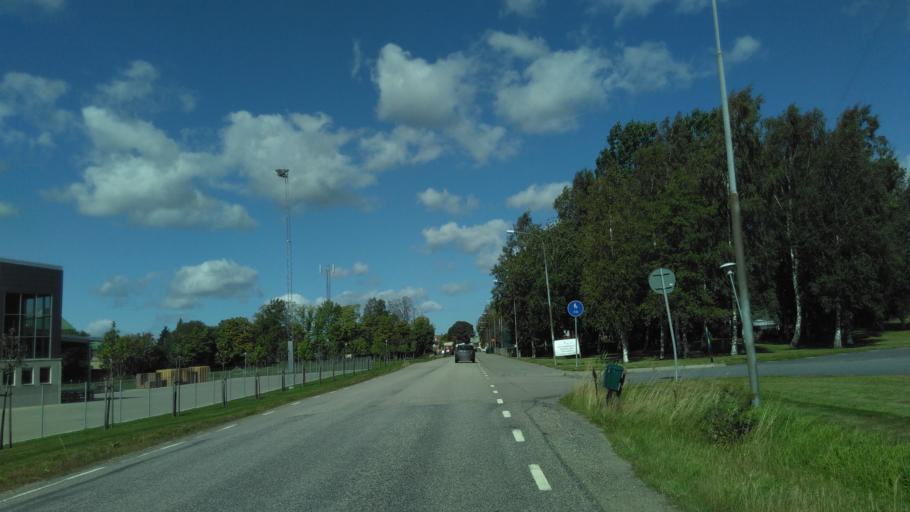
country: SE
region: Vaestra Goetaland
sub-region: Herrljunga Kommun
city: Herrljunga
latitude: 58.1671
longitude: 13.0019
